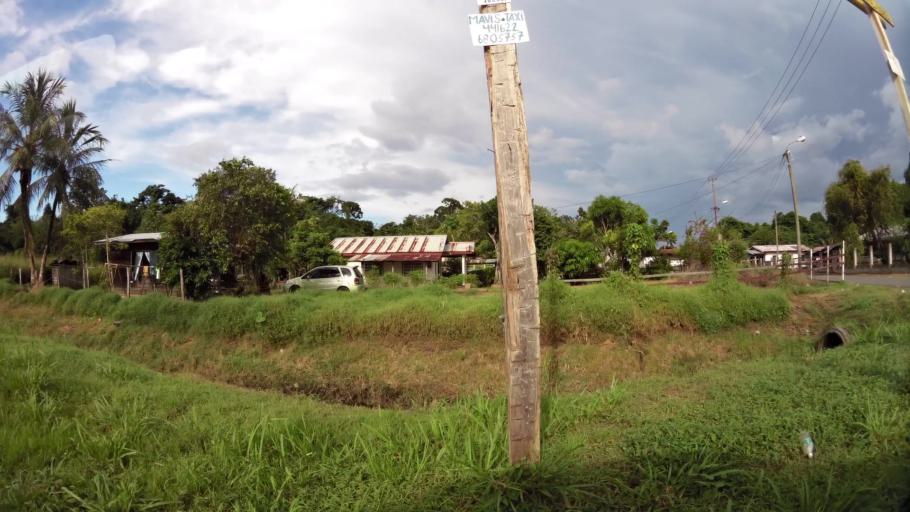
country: SR
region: Paramaribo
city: Paramaribo
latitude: 5.8462
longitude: -55.1773
